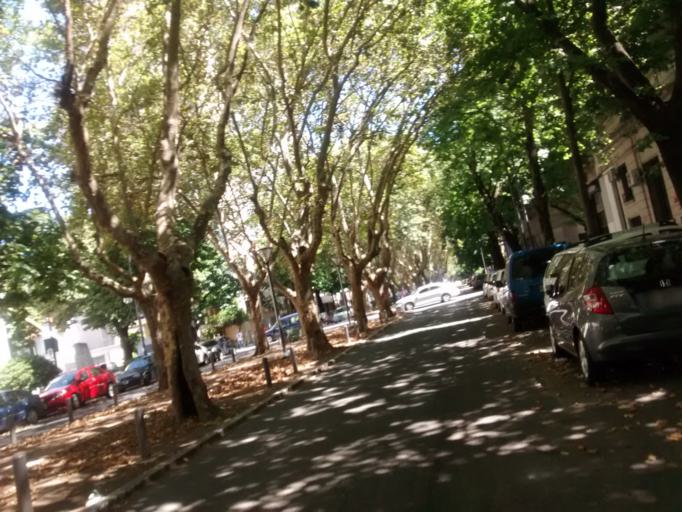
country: AR
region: Buenos Aires
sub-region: Partido de La Plata
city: La Plata
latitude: -34.9112
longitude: -57.9446
